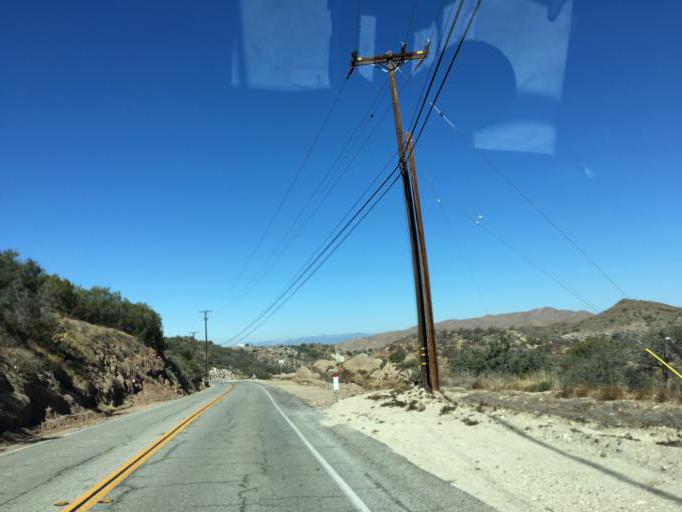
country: US
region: California
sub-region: Los Angeles County
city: Agua Dulce
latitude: 34.4771
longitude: -118.3511
